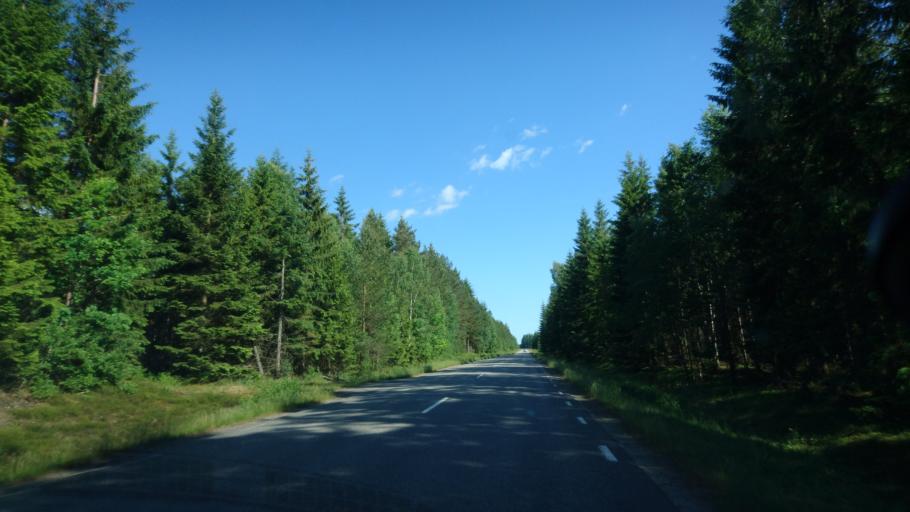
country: SE
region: Skane
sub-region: Osby Kommun
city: Lonsboda
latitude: 56.4380
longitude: 14.2505
